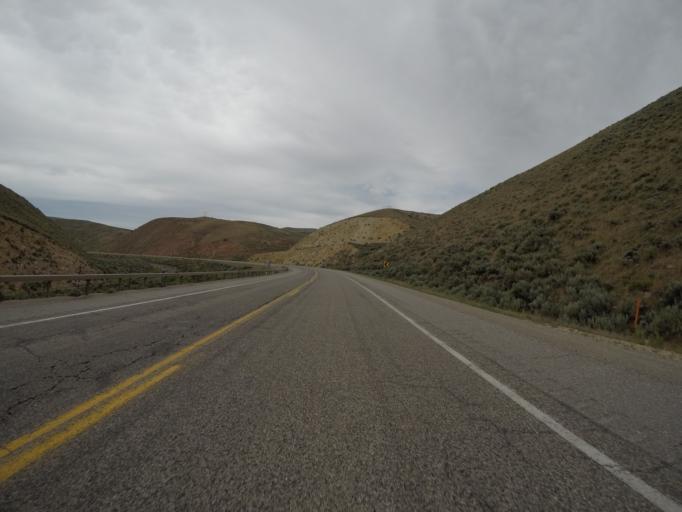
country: US
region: Wyoming
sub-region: Lincoln County
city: Kemmerer
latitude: 41.8230
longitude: -110.8084
